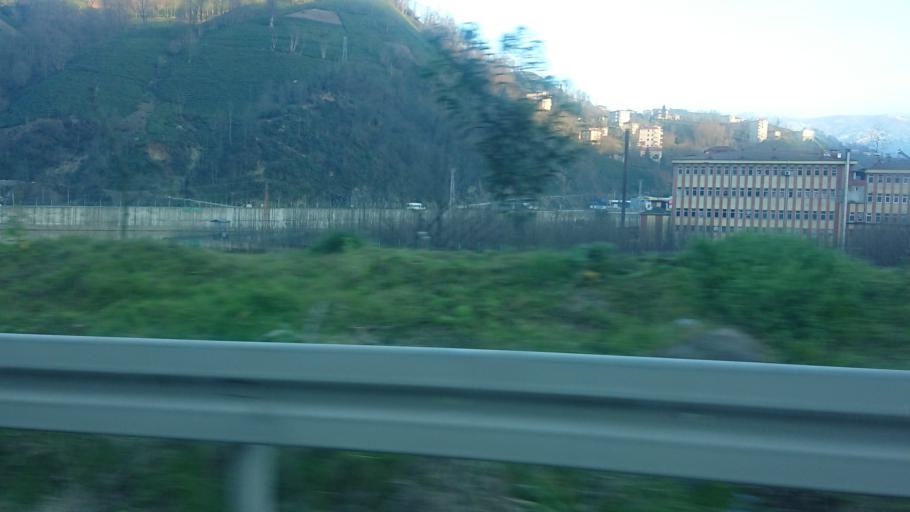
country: TR
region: Rize
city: Gundogdu
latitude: 41.0206
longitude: 40.5748
